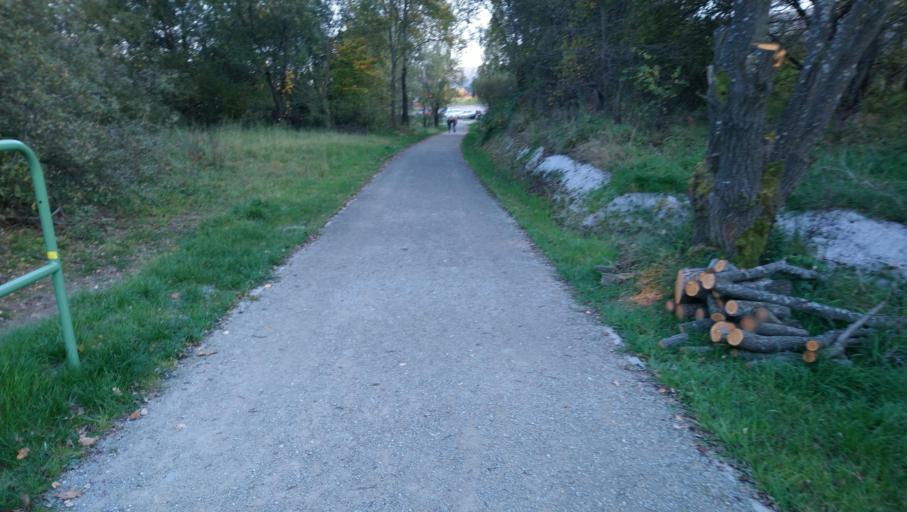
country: PL
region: Lesser Poland Voivodeship
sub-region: Powiat gorlicki
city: Ropa
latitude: 49.5500
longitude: 21.0848
